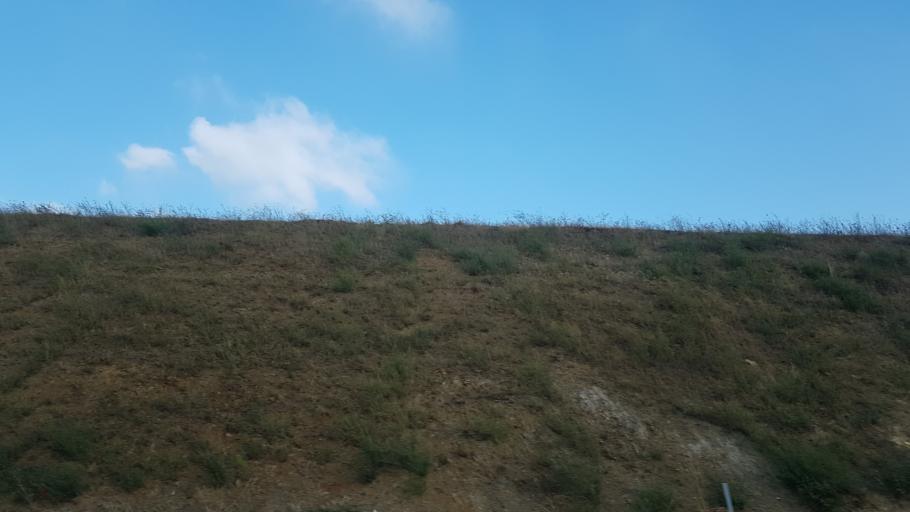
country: TR
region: Balikesir
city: Yenikoy
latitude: 39.7684
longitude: 28.0070
